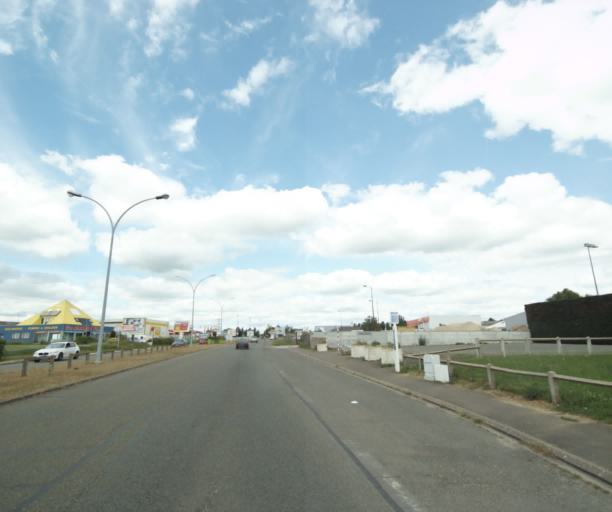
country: FR
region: Centre
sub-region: Departement d'Eure-et-Loir
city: Mainvilliers
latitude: 48.4448
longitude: 1.4512
